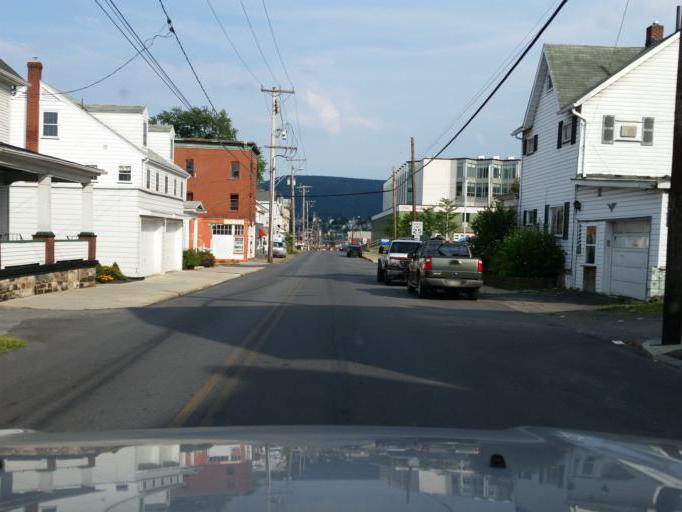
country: US
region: Pennsylvania
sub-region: Blair County
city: Altoona
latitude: 40.5244
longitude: -78.3988
